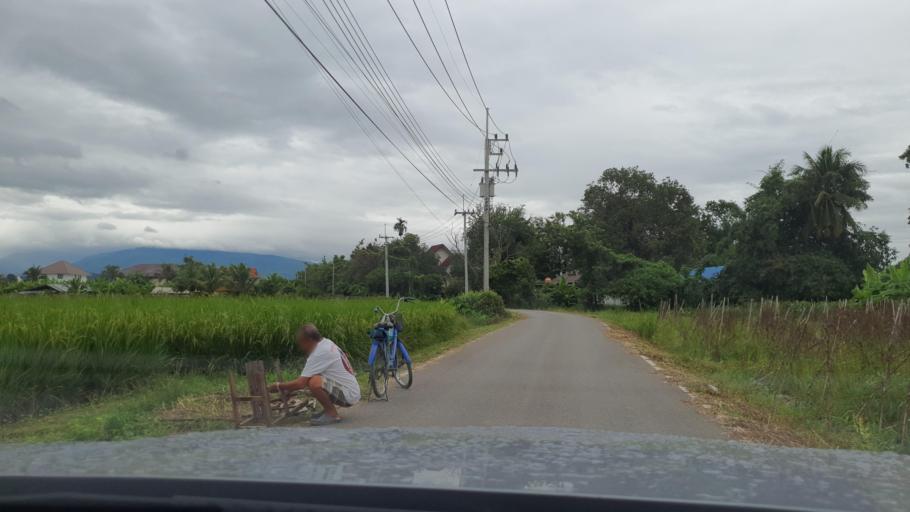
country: TH
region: Chiang Mai
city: Hang Dong
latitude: 18.6647
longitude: 98.9077
